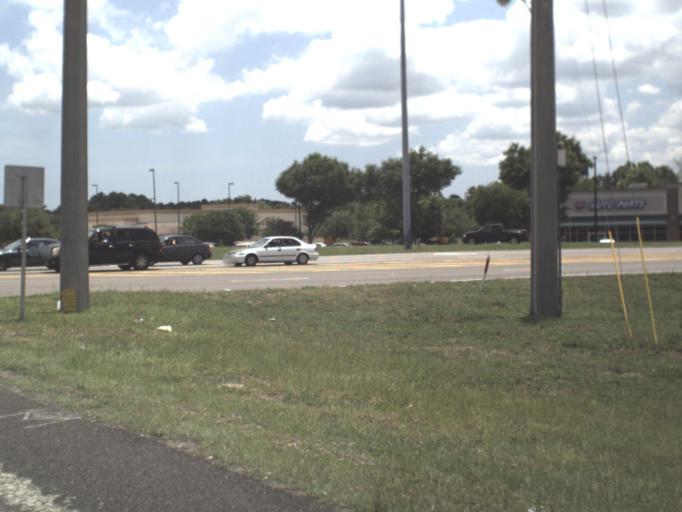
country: US
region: Florida
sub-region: Duval County
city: Jacksonville
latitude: 30.3213
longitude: -81.5519
